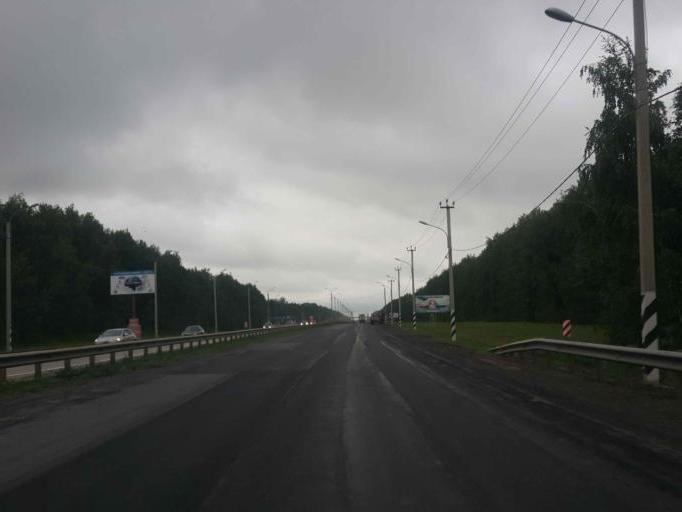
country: RU
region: Tambov
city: Selezni
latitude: 52.7563
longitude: 41.1557
